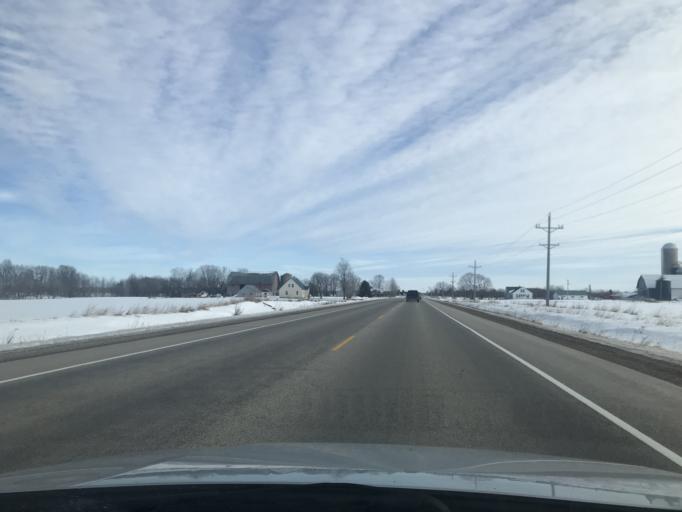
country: US
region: Wisconsin
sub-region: Oconto County
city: Gillett
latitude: 44.8962
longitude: -88.2570
